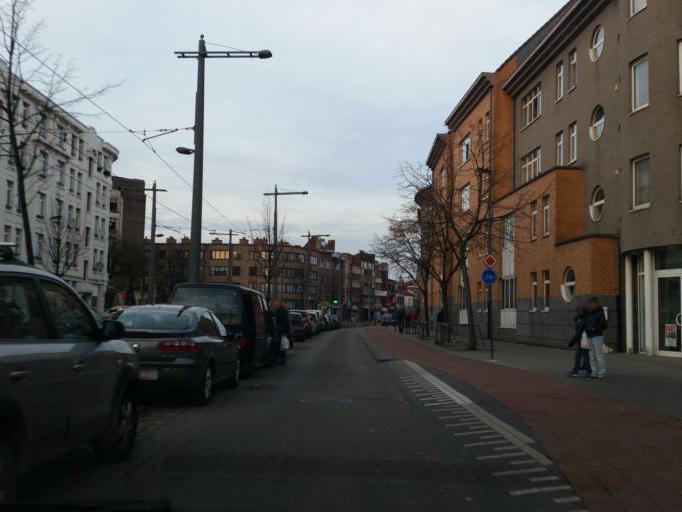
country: BE
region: Flanders
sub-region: Provincie Antwerpen
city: Hoboken
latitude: 51.1878
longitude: 4.3762
